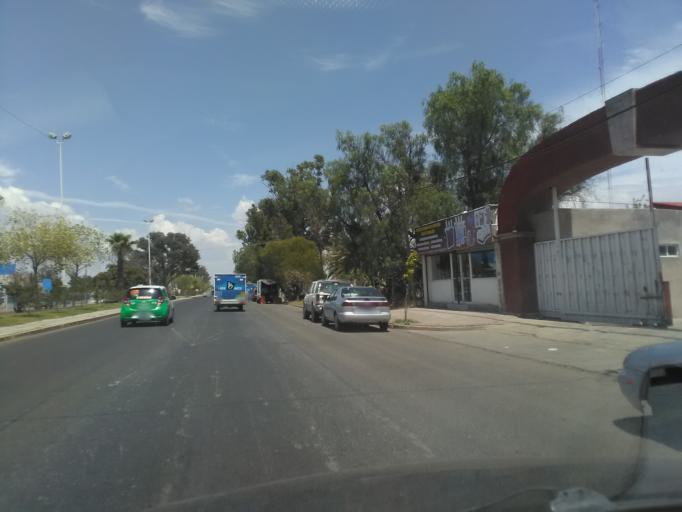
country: MX
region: Durango
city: Victoria de Durango
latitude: 24.0309
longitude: -104.6183
